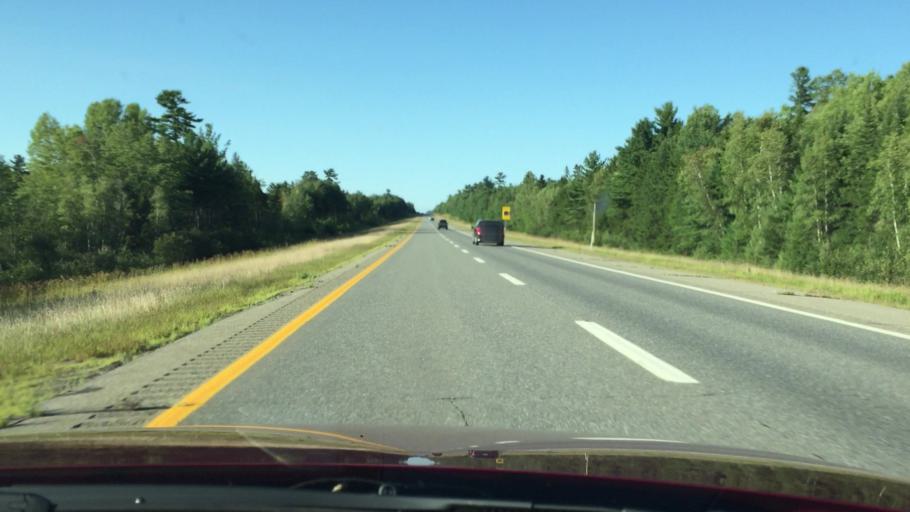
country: US
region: Maine
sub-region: Penobscot County
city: Lincoln
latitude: 45.3996
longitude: -68.5988
